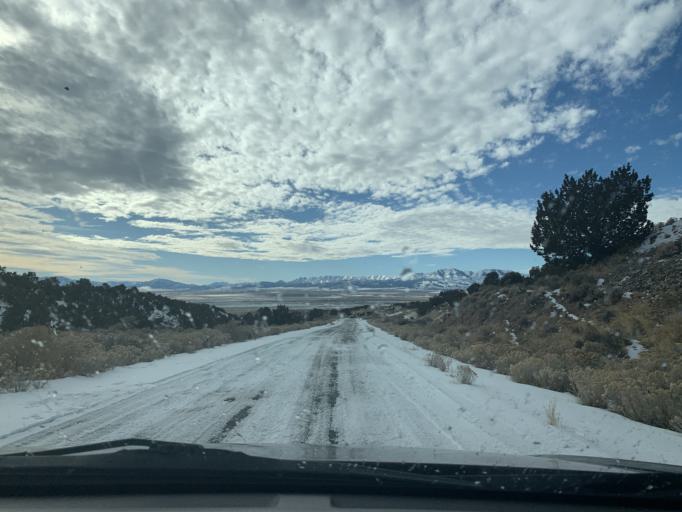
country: US
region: Utah
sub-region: Tooele County
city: Tooele
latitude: 40.3075
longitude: -112.2557
